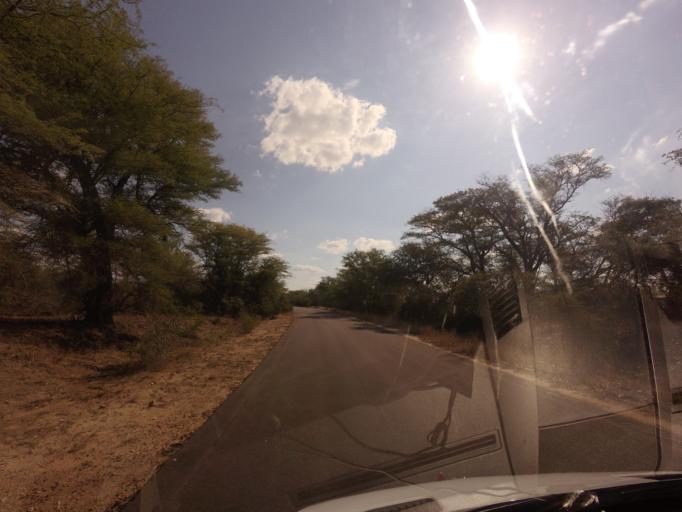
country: ZA
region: Limpopo
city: Thulamahashi
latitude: -24.4165
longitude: 31.5155
